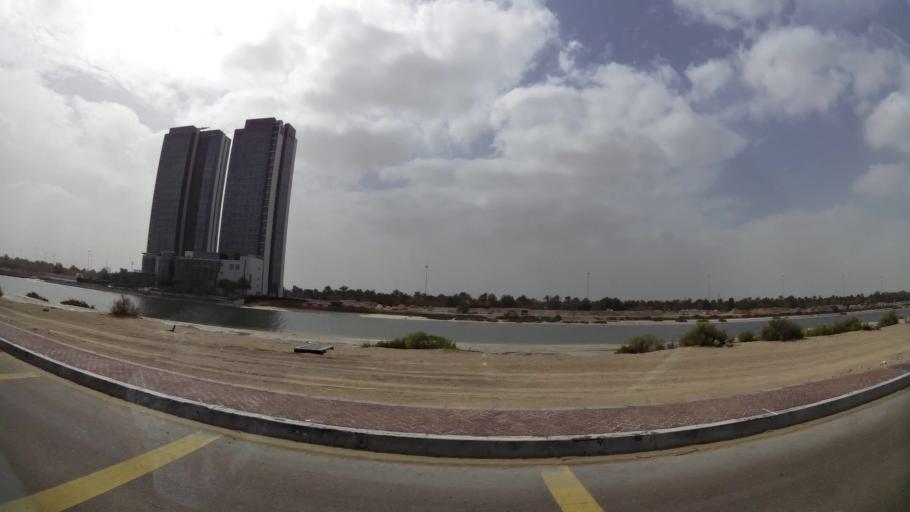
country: AE
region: Abu Dhabi
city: Abu Dhabi
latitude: 24.3980
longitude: 54.5173
